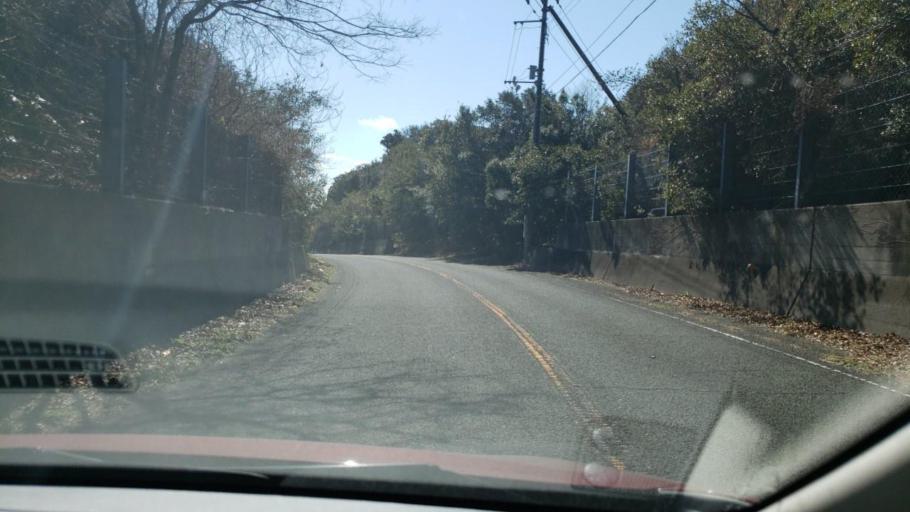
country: JP
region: Tokushima
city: Narutocho-mitsuishi
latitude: 34.2297
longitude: 134.6004
